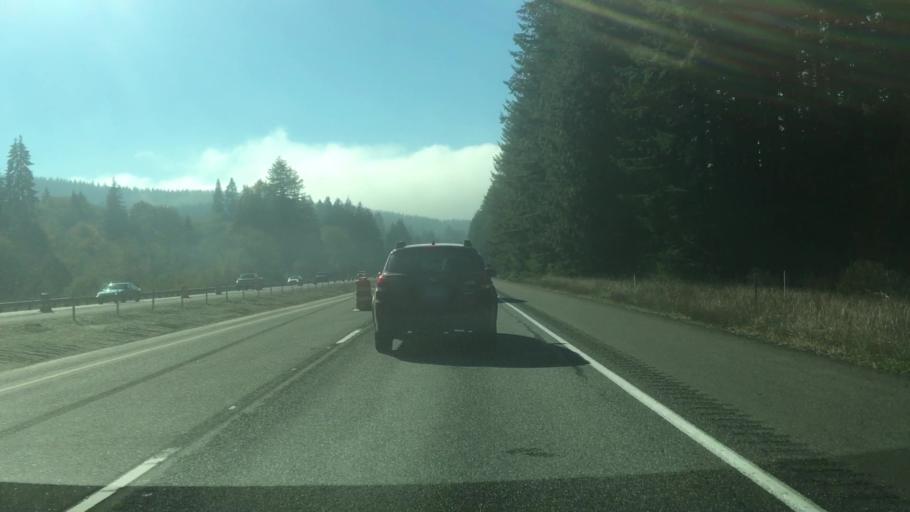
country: US
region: Washington
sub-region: Grays Harbor County
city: McCleary
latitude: 47.0464
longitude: -123.3122
